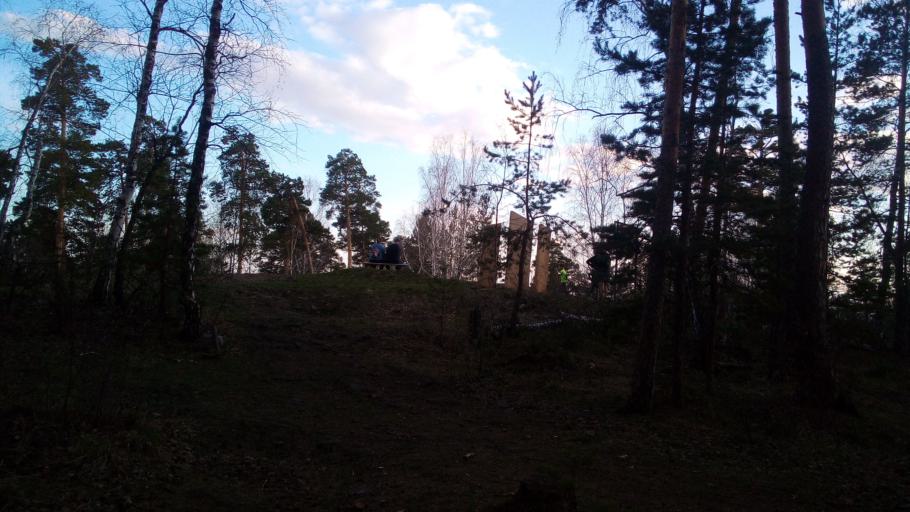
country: RU
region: Chelyabinsk
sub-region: Gorod Chelyabinsk
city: Chelyabinsk
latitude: 55.1601
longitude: 61.3230
